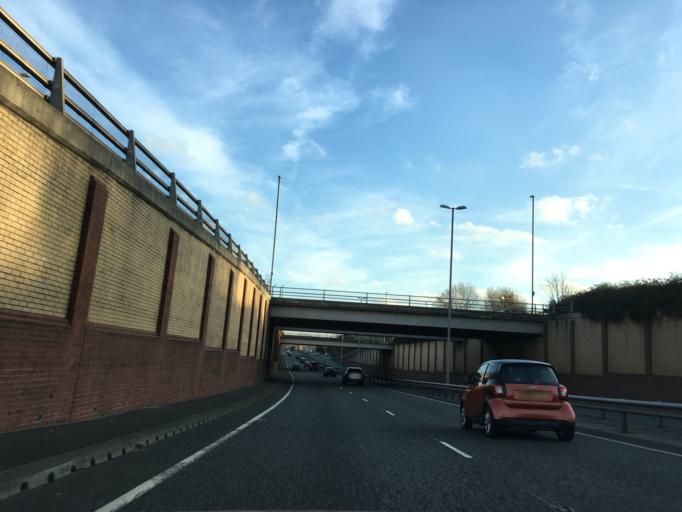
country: GB
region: England
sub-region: Borough of Stockport
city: Cheadle Hulme
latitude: 53.3807
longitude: -2.2194
